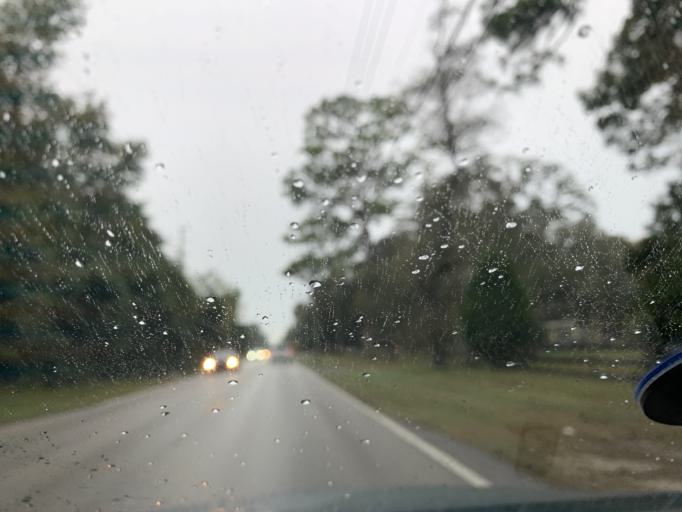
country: US
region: Florida
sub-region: Hernando County
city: Masaryktown
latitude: 28.4338
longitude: -82.4678
